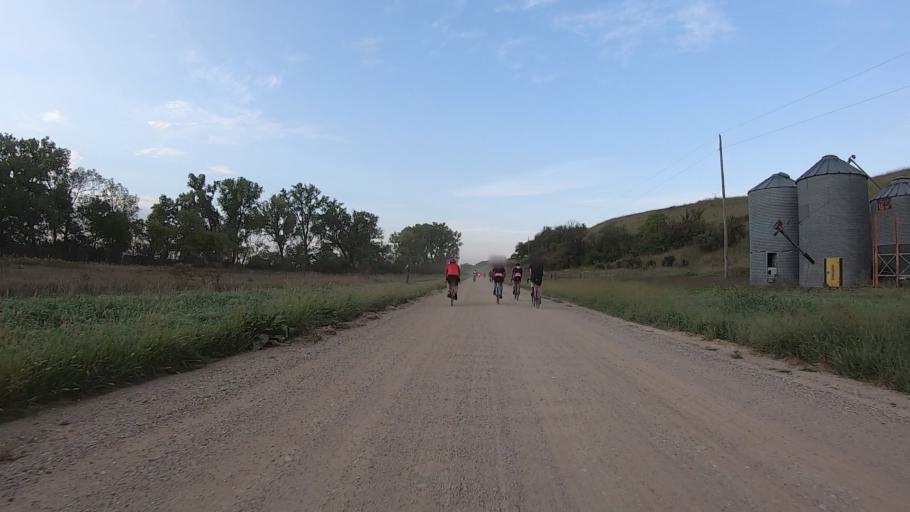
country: US
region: Kansas
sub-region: Marshall County
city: Marysville
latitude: 39.8298
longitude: -96.6648
